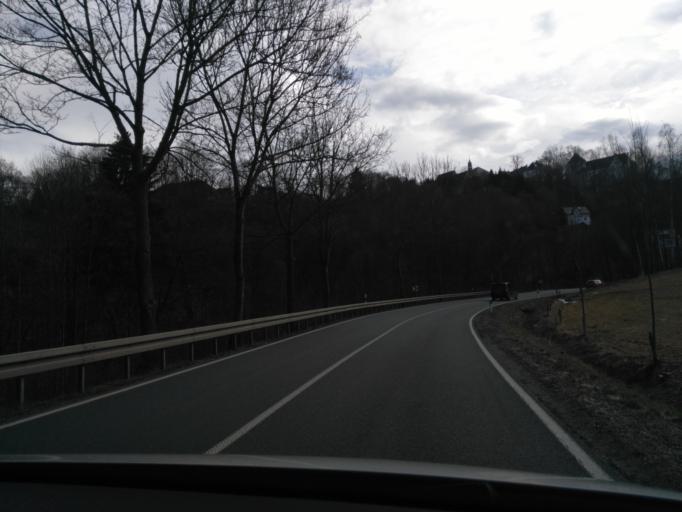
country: DE
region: Saxony
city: Wolkenstein
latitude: 50.6577
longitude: 13.0601
